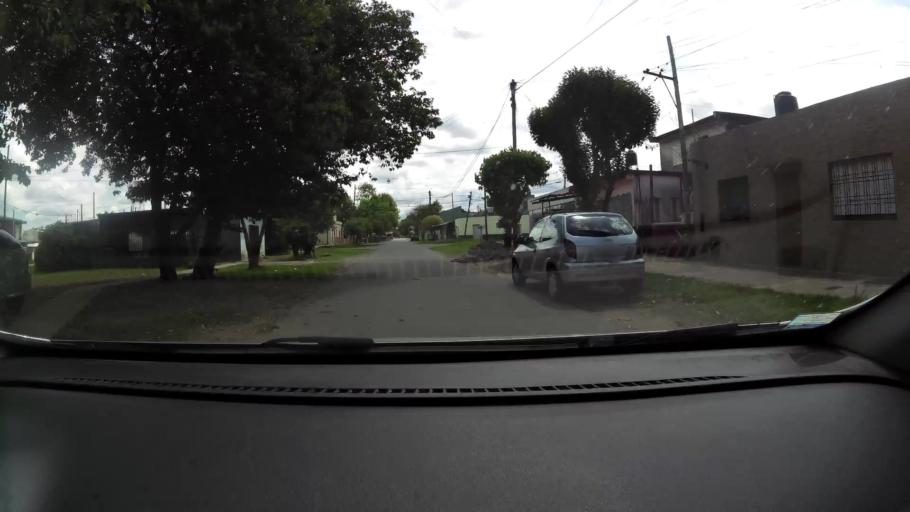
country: AR
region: Santa Fe
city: Gobernador Galvez
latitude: -33.0116
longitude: -60.6370
